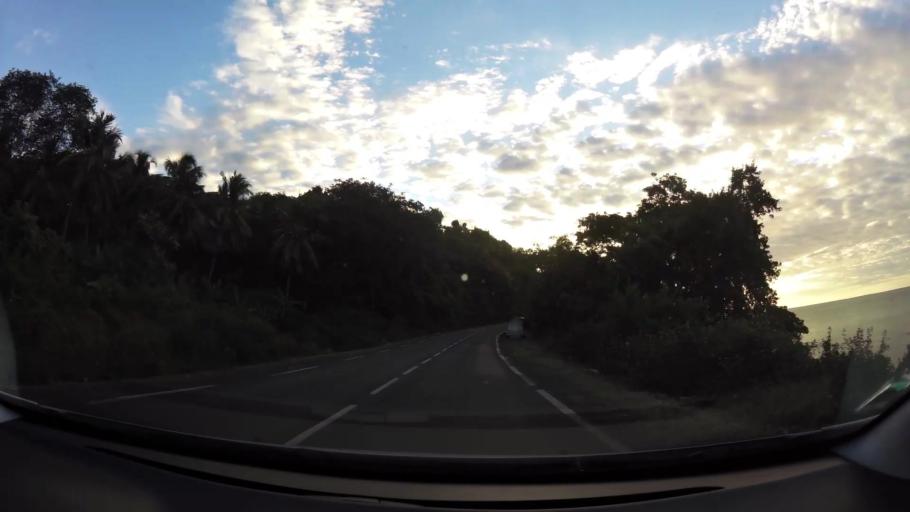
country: YT
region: Koungou
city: Koungou
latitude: -12.7295
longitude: 45.1913
